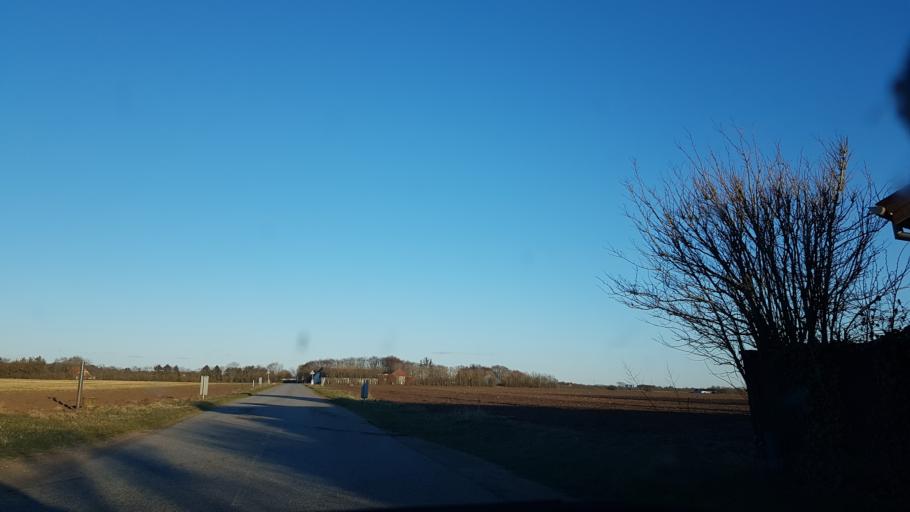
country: DK
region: South Denmark
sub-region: Esbjerg Kommune
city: Ribe
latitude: 55.3842
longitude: 8.7467
